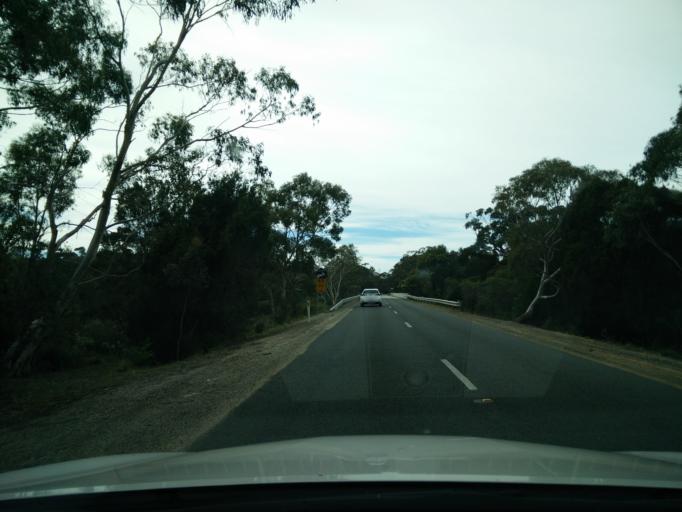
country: AU
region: Tasmania
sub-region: Break O'Day
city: St Helens
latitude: -41.9418
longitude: 148.2313
